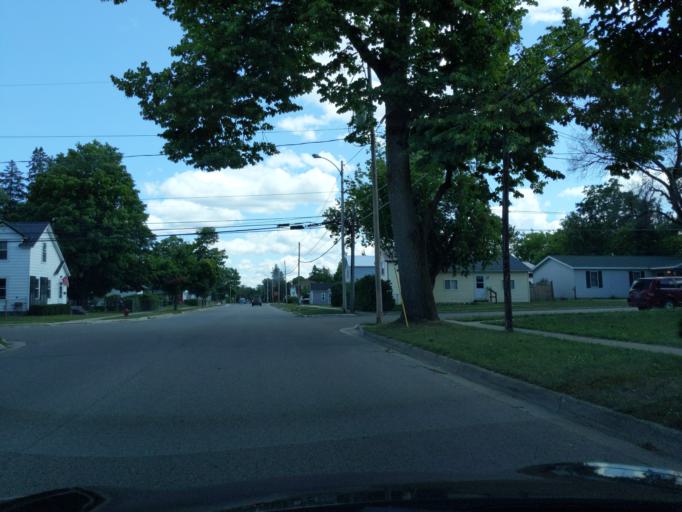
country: US
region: Michigan
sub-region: Crawford County
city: Grayling
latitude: 44.6651
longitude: -84.7128
